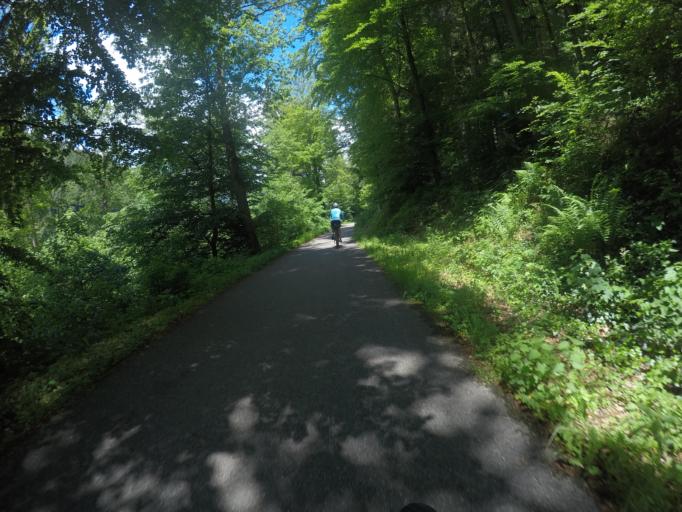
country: DE
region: Baden-Wuerttemberg
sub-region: Karlsruhe Region
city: Bad Liebenzell
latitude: 48.7663
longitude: 8.7313
